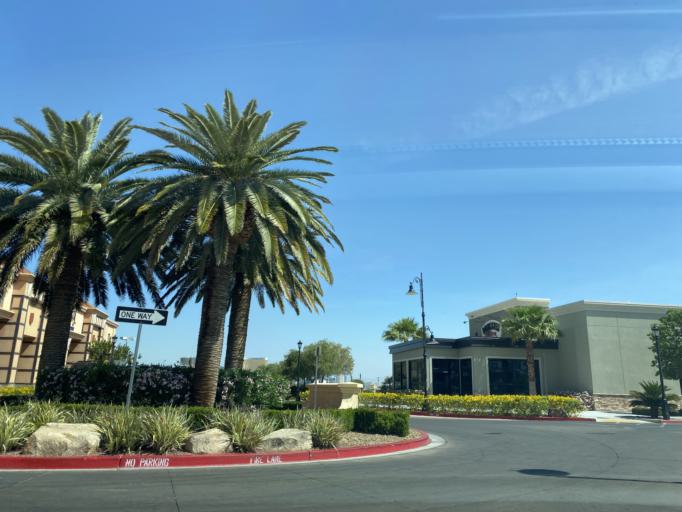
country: US
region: Nevada
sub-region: Clark County
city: Paradise
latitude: 36.0697
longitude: -115.1751
